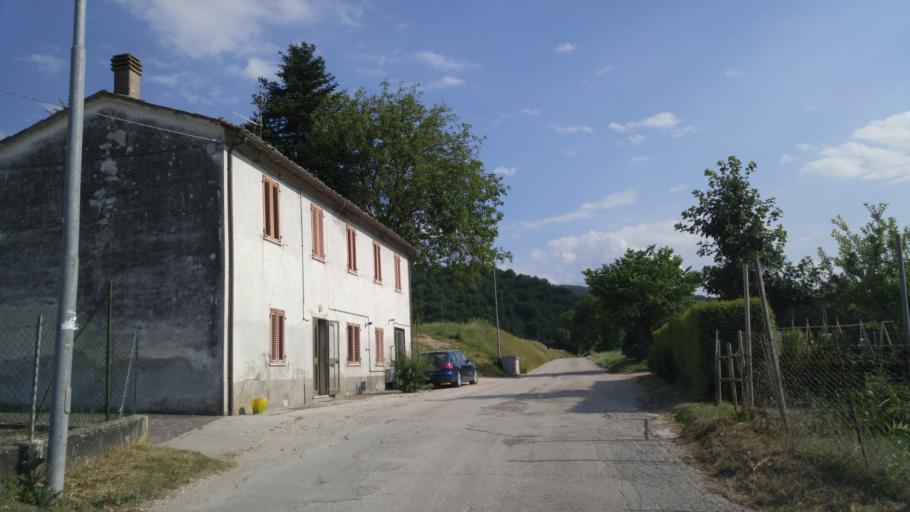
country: IT
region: The Marches
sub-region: Provincia di Pesaro e Urbino
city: Acqualagna
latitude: 43.6274
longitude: 12.6865
